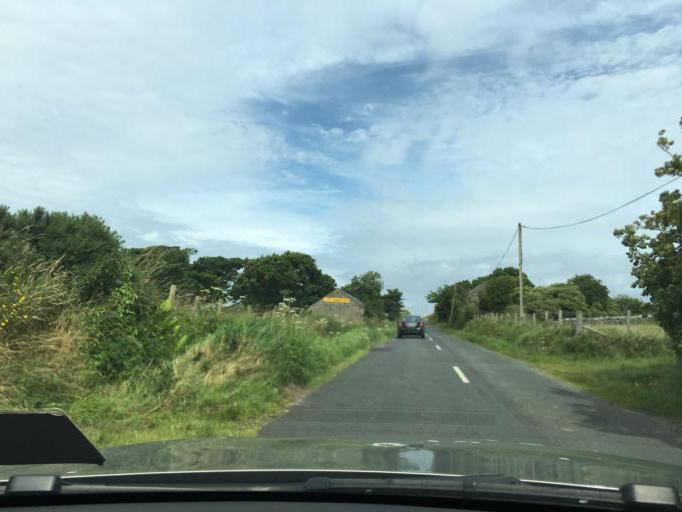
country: IE
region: Ulster
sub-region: County Donegal
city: Carndonagh
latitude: 55.3462
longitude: -7.3156
